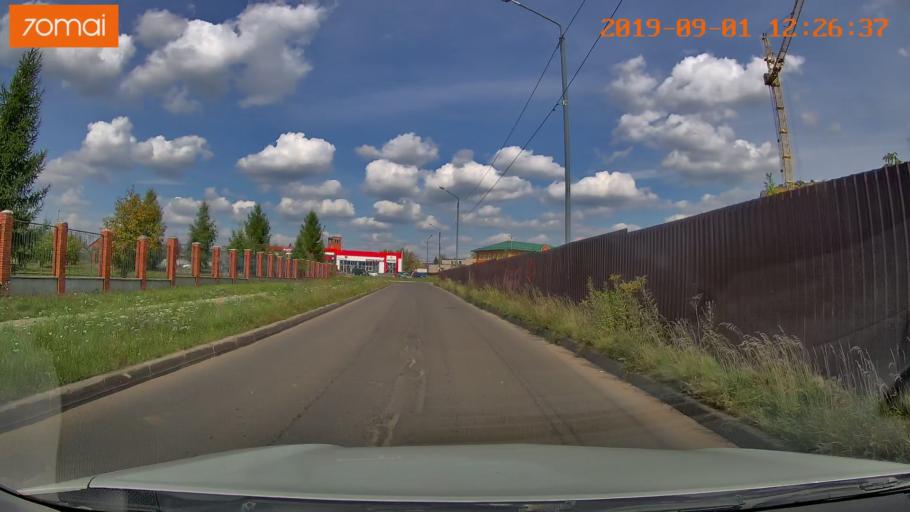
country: RU
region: Kaluga
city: Maloyaroslavets
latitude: 55.0024
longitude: 36.4615
